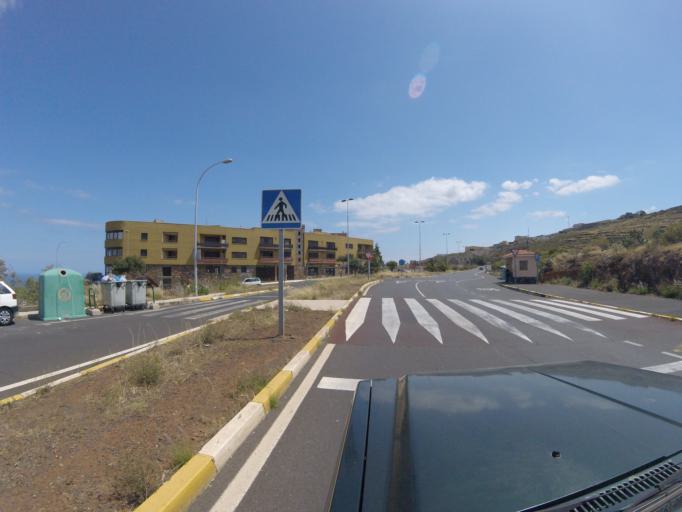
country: ES
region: Canary Islands
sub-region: Provincia de Santa Cruz de Tenerife
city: La Laguna
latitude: 28.4339
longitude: -16.3109
